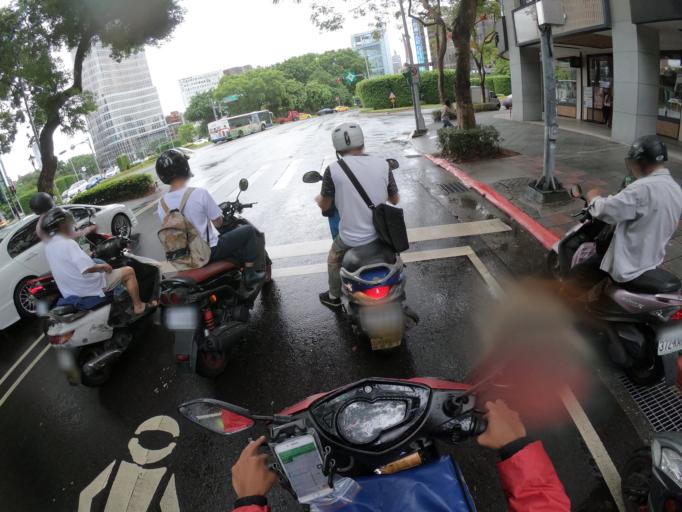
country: TW
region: Taipei
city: Taipei
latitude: 25.0389
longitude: 121.5486
